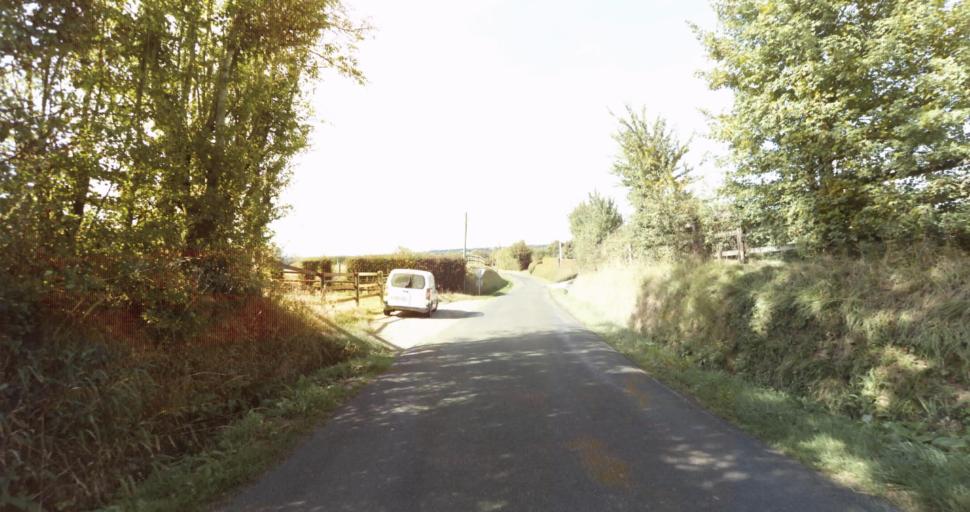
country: FR
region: Lower Normandy
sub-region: Departement de l'Orne
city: Gace
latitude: 48.7210
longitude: 0.2296
